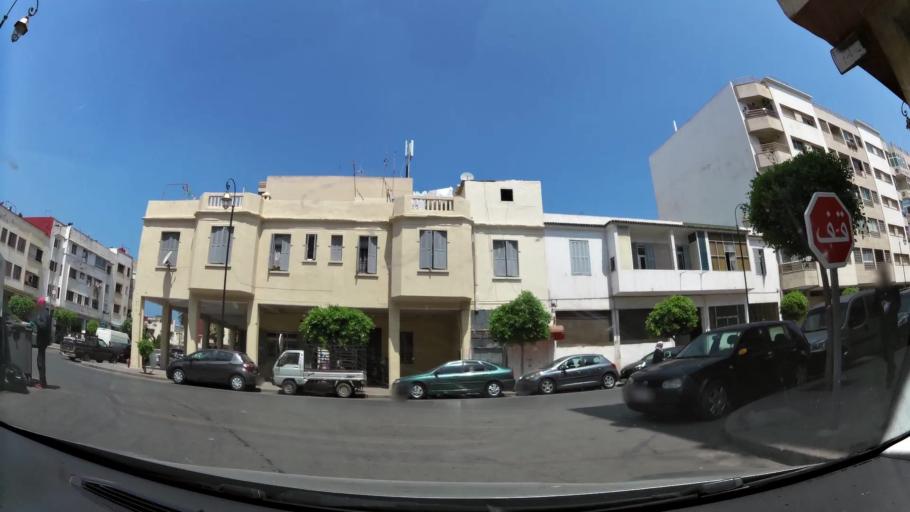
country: MA
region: Rabat-Sale-Zemmour-Zaer
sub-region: Rabat
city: Rabat
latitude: 34.0226
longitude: -6.8493
